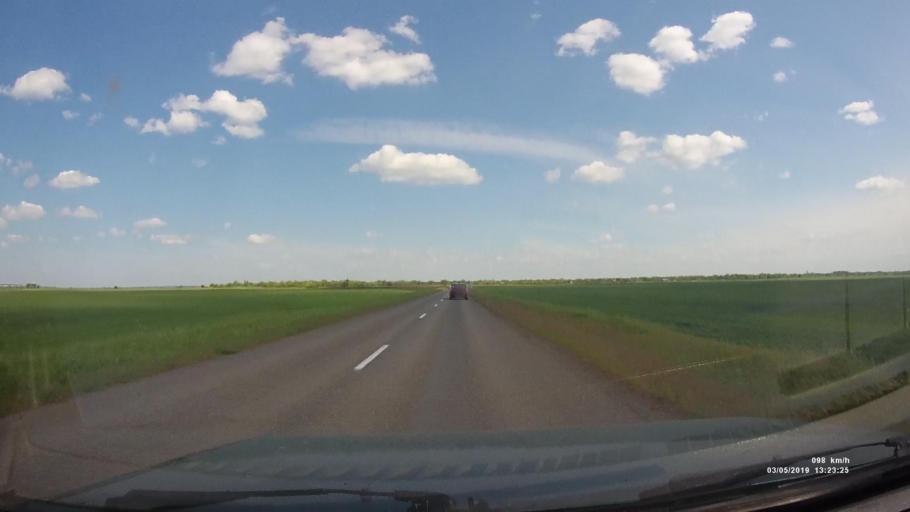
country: RU
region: Rostov
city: Semikarakorsk
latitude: 47.5625
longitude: 40.7818
